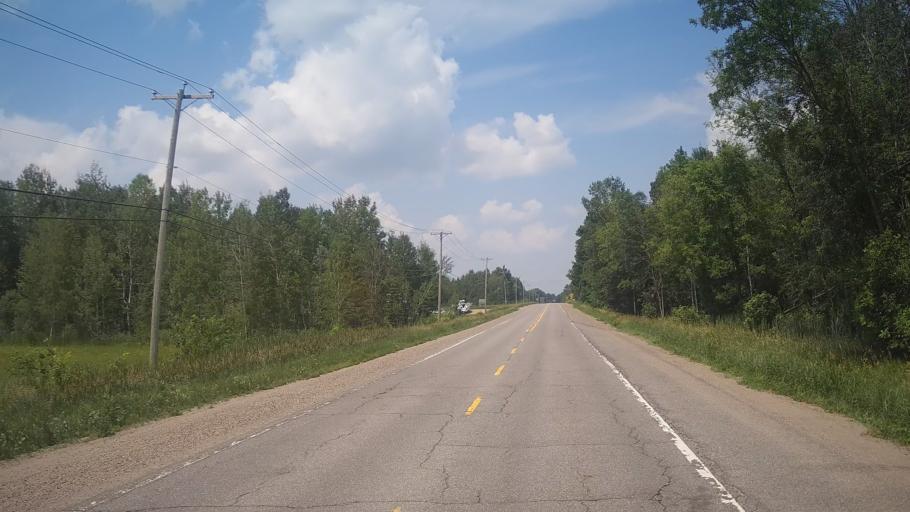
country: CA
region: Quebec
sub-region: Outaouais
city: Shawville
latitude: 45.5702
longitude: -76.4349
